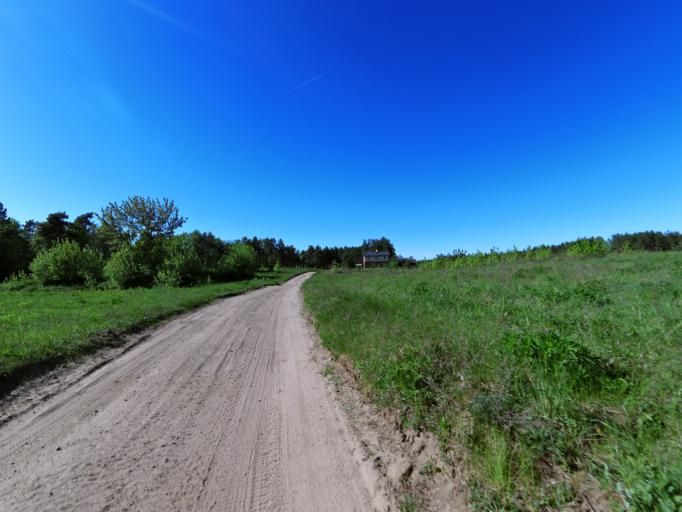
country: LT
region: Vilnius County
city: Pilaite
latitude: 54.6845
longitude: 25.1616
